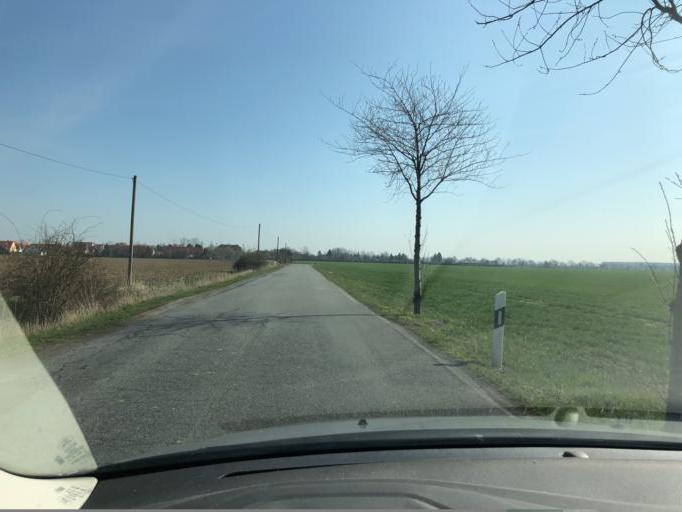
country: DE
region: Saxony
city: Krostitz
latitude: 51.4197
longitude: 12.4338
